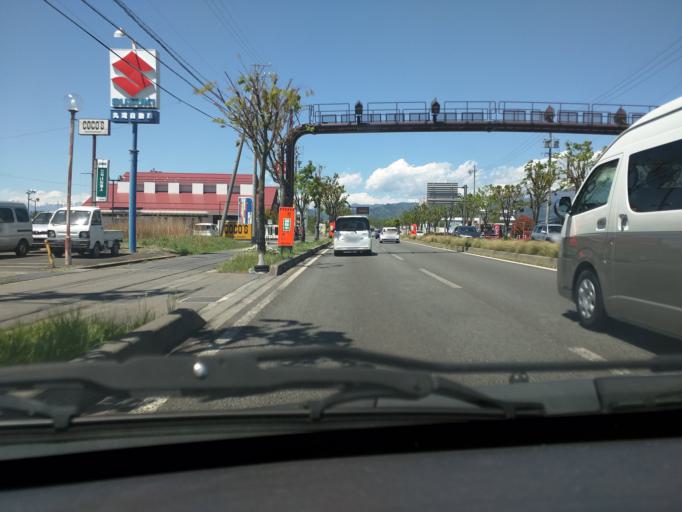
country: JP
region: Nagano
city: Suzaka
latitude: 36.6378
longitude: 138.2700
